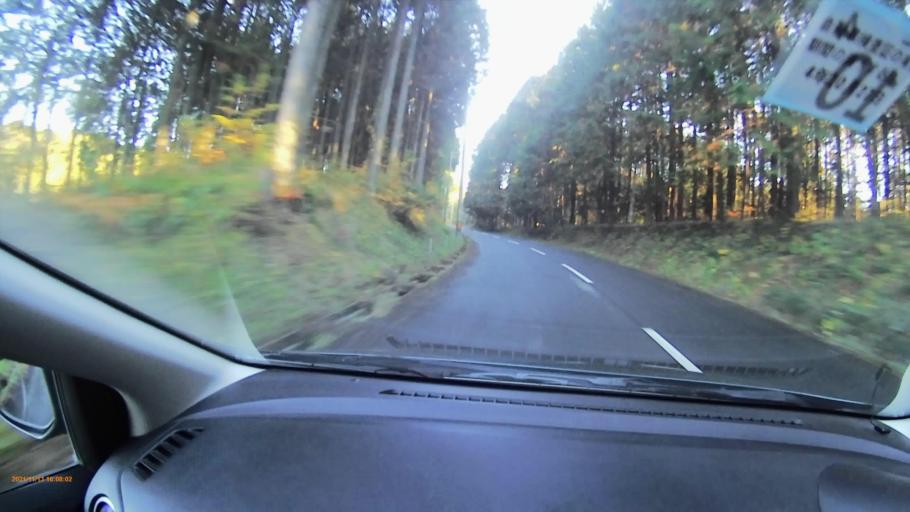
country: JP
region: Gifu
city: Nakatsugawa
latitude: 35.5955
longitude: 137.4812
